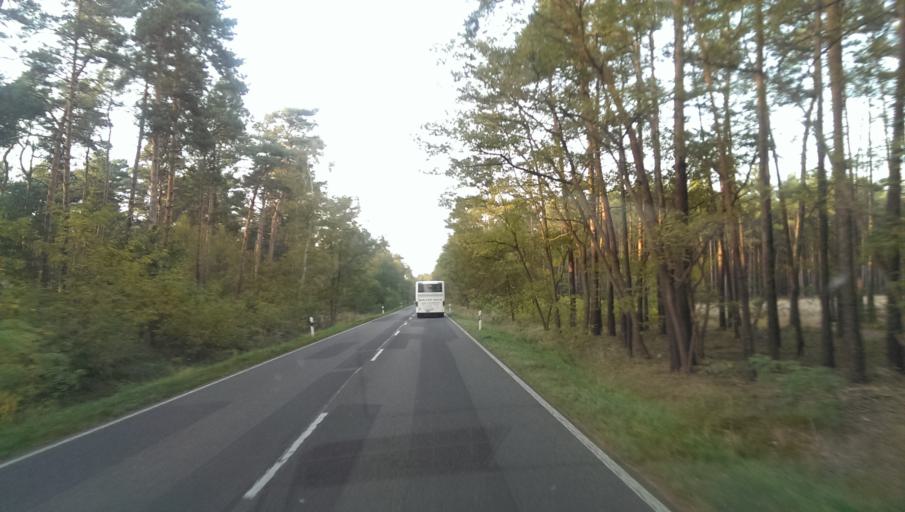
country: DE
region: Saxony-Anhalt
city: Holzdorf
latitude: 51.7774
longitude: 13.1959
